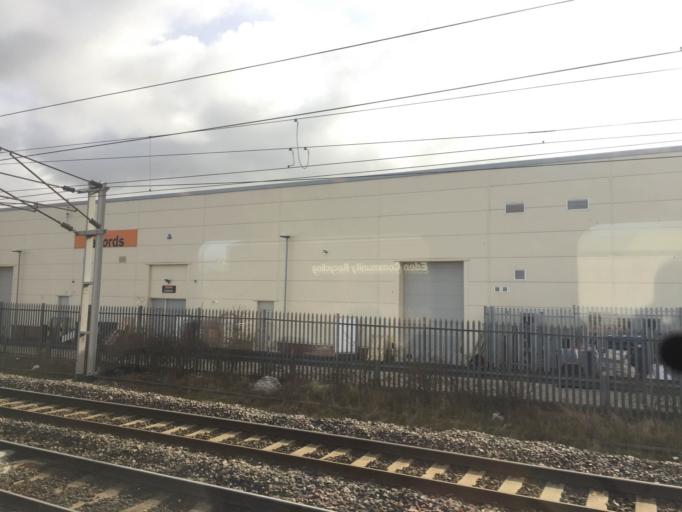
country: GB
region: England
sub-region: Cumbria
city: Penrith
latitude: 54.6592
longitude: -2.7611
